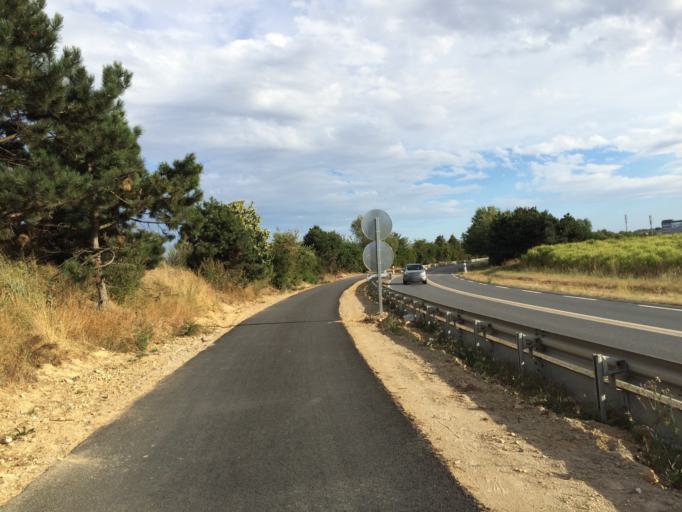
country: FR
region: Ile-de-France
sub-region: Departement de l'Essonne
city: Paray-Vieille-Poste
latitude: 48.7123
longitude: 2.3516
